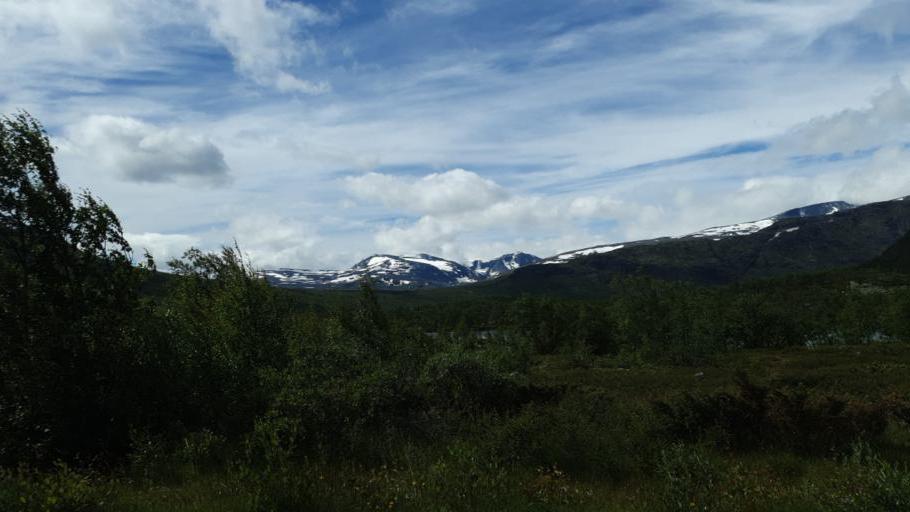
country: NO
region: Oppland
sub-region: Oystre Slidre
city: Heggenes
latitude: 61.4875
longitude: 8.8296
